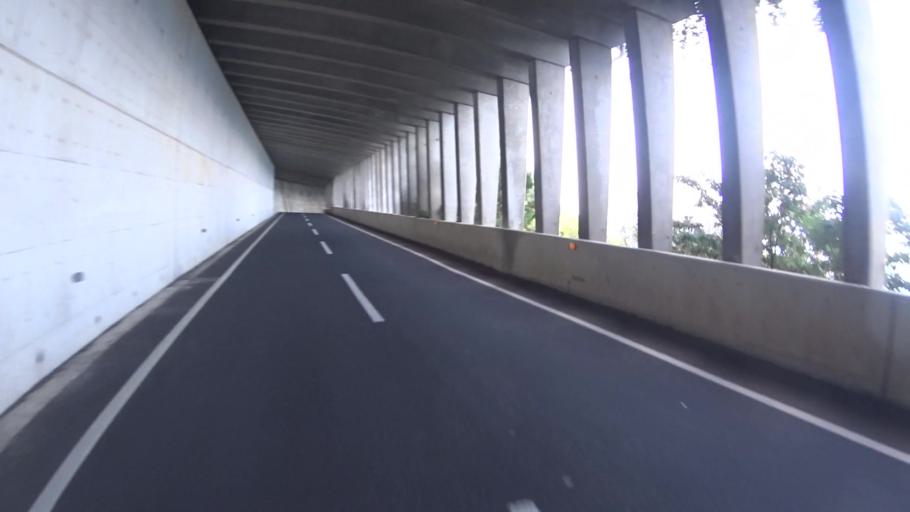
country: JP
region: Kyoto
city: Miyazu
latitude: 35.7622
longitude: 135.2393
